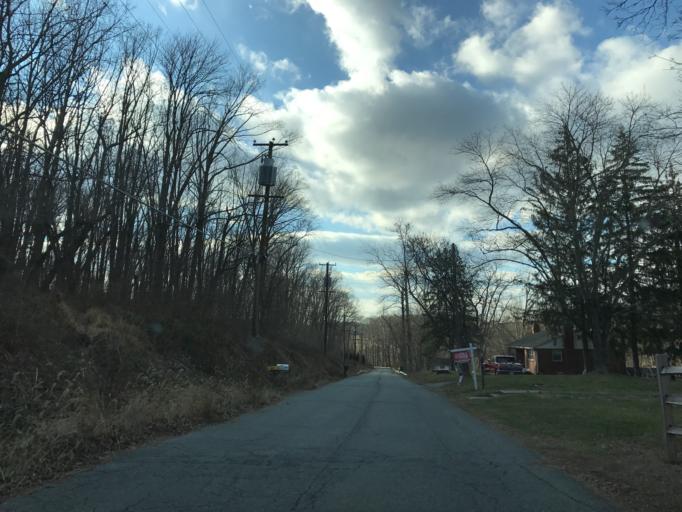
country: US
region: Maryland
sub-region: Cecil County
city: Rising Sun
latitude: 39.6938
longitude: -76.1191
